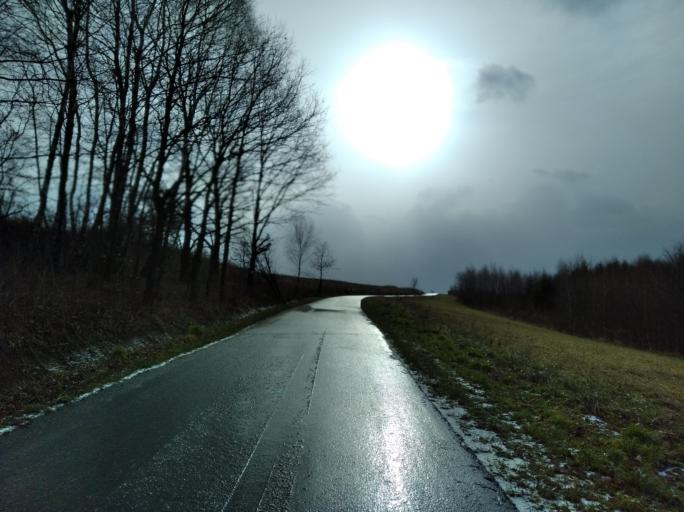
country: PL
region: Subcarpathian Voivodeship
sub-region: Powiat strzyzowski
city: Wysoka Strzyzowska
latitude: 49.8851
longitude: 21.7282
